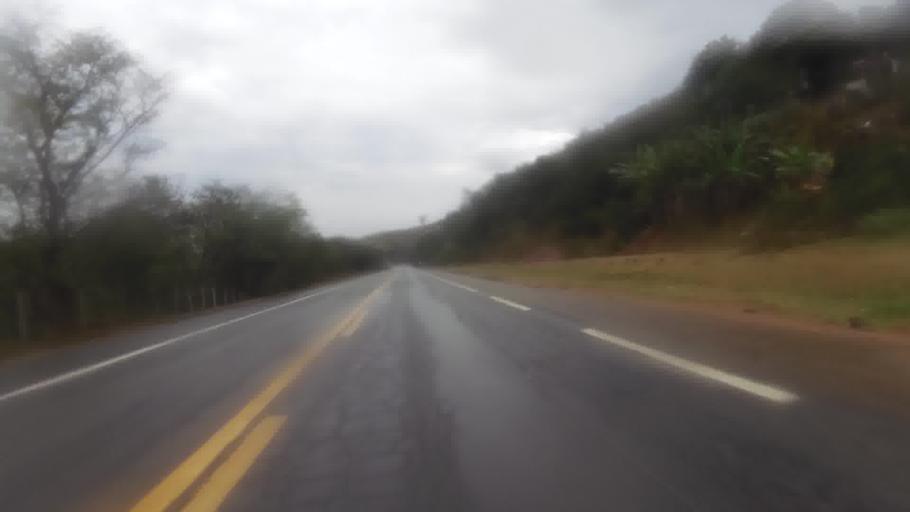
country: BR
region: Espirito Santo
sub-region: Cachoeiro De Itapemirim
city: Cachoeiro de Itapemirim
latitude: -21.0194
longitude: -41.1523
